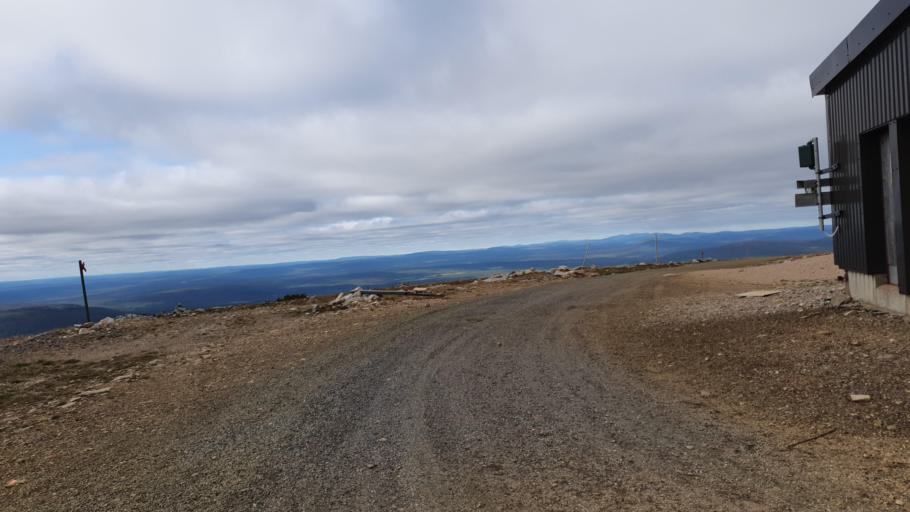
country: FI
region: Lapland
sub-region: Tunturi-Lappi
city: Kolari
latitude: 67.5668
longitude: 24.2093
